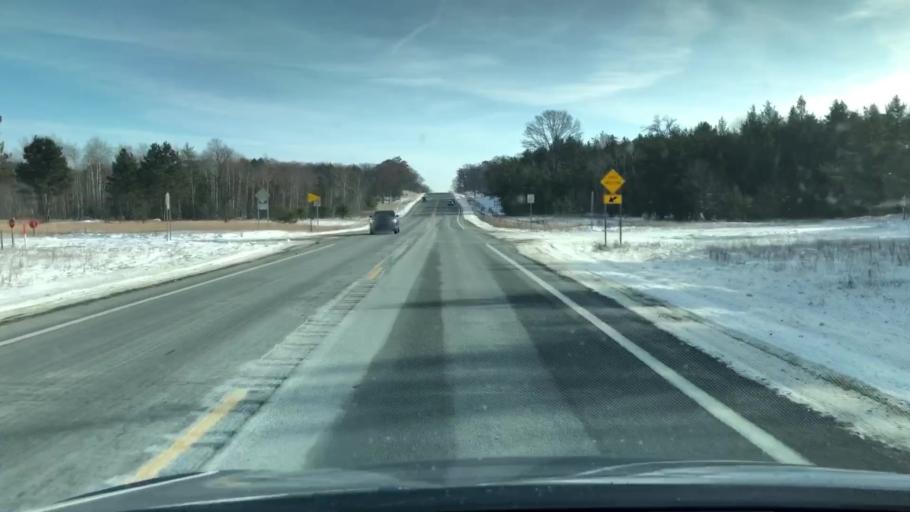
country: US
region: Michigan
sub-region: Crawford County
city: Grayling
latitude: 44.7029
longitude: -84.8989
